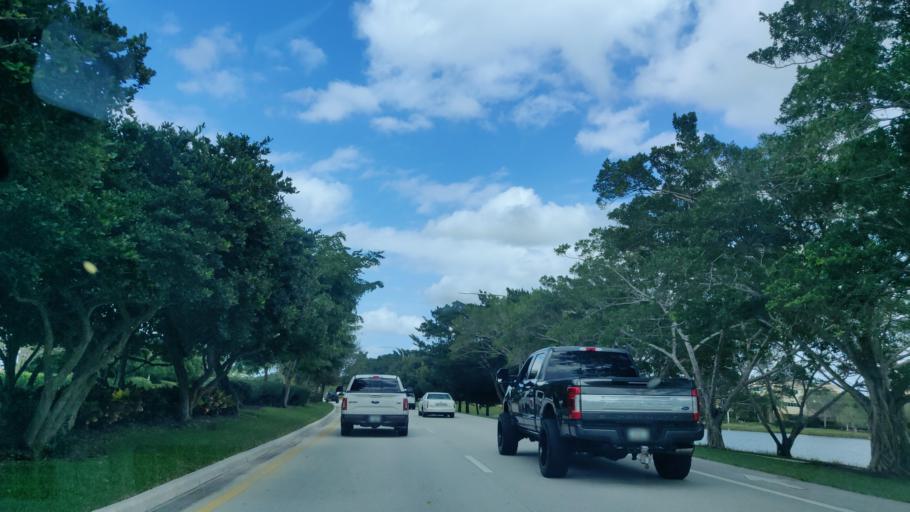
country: US
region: Florida
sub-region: Broward County
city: Weston
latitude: 26.0976
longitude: -80.3688
